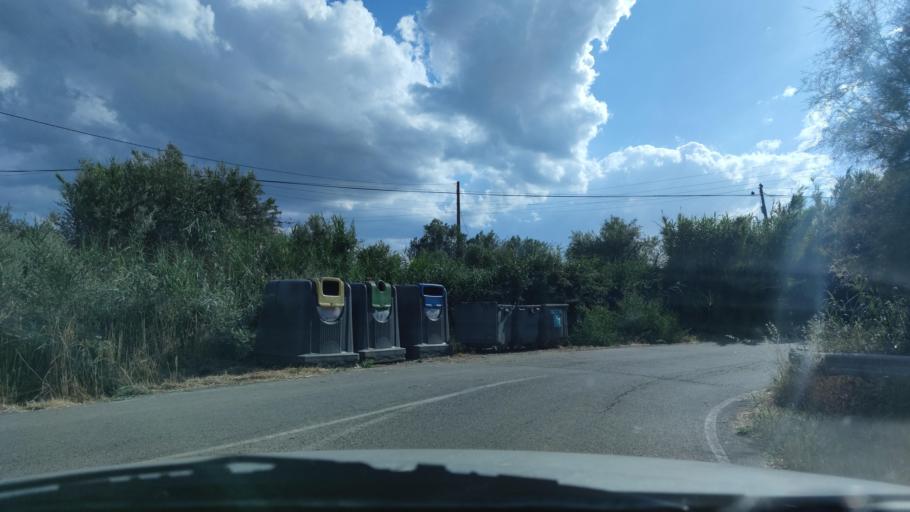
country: ES
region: Catalonia
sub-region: Provincia de Lleida
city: Alpicat
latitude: 41.6219
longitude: 0.5746
